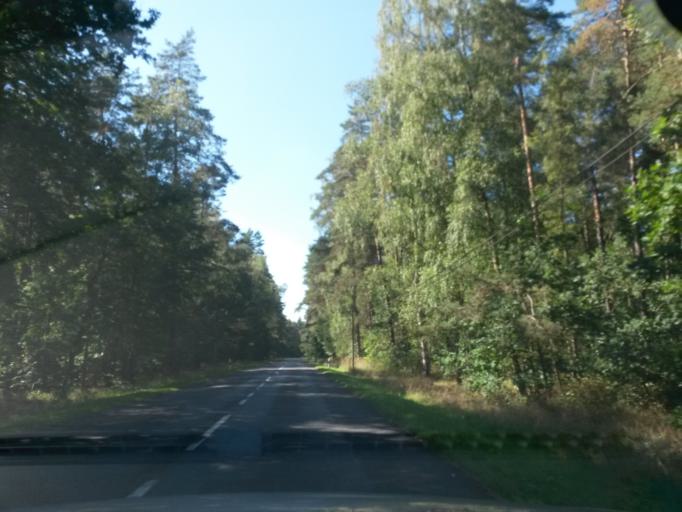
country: DE
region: Brandenburg
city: Lychen
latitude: 53.2221
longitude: 13.3506
